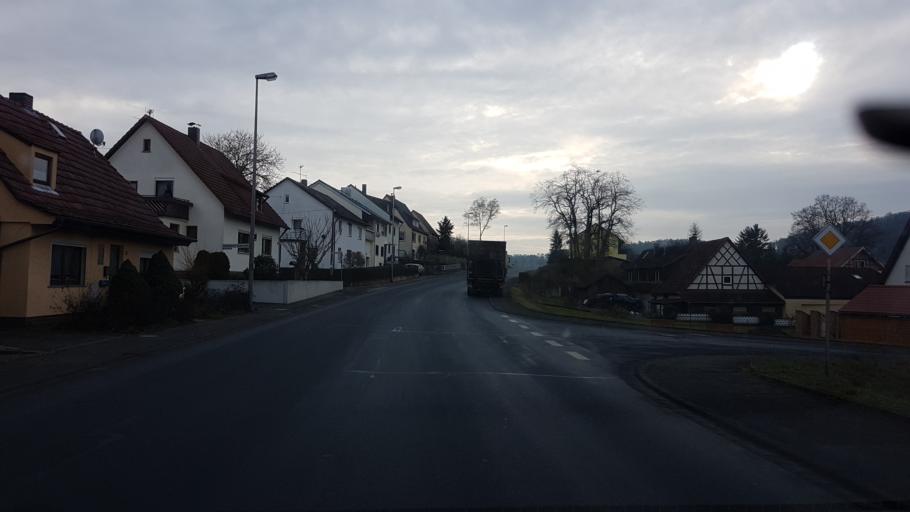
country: DE
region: Bavaria
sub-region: Regierungsbezirk Unterfranken
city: Pfarrweisach
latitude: 50.1693
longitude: 10.7191
